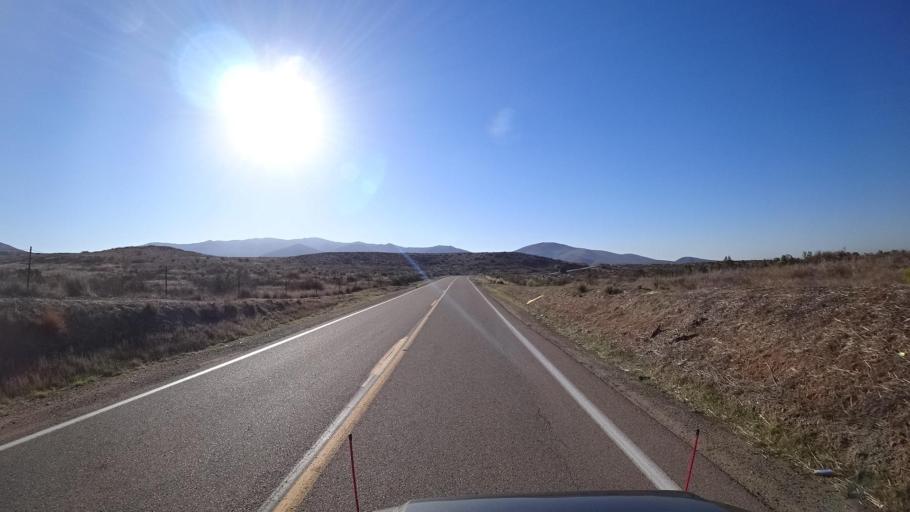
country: US
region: California
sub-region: San Diego County
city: Jamul
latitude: 32.6410
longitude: -116.9238
